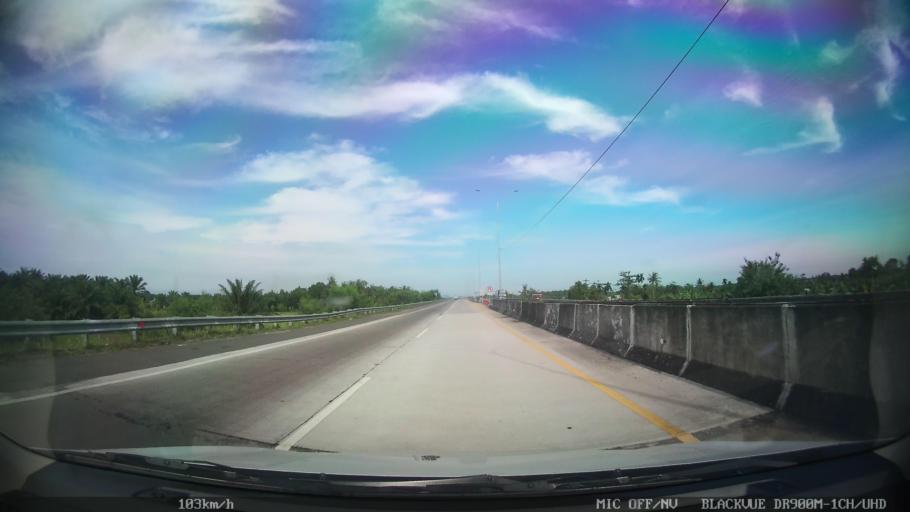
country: ID
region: North Sumatra
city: Sunggal
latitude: 3.6387
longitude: 98.5750
